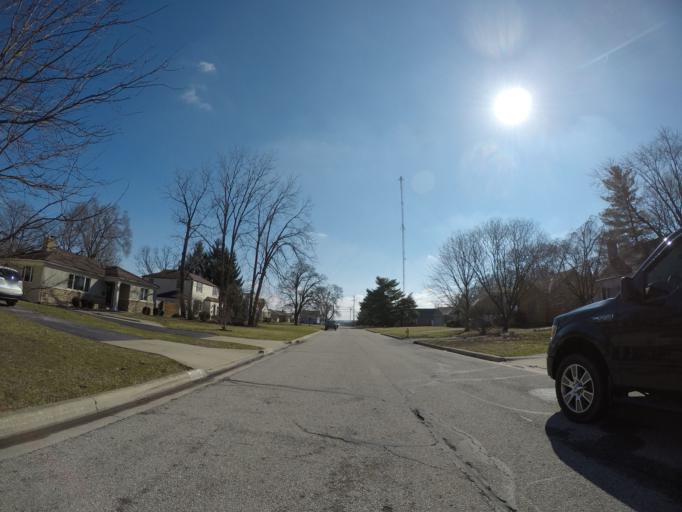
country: US
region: Ohio
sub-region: Franklin County
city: Upper Arlington
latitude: 40.0092
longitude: -83.0499
